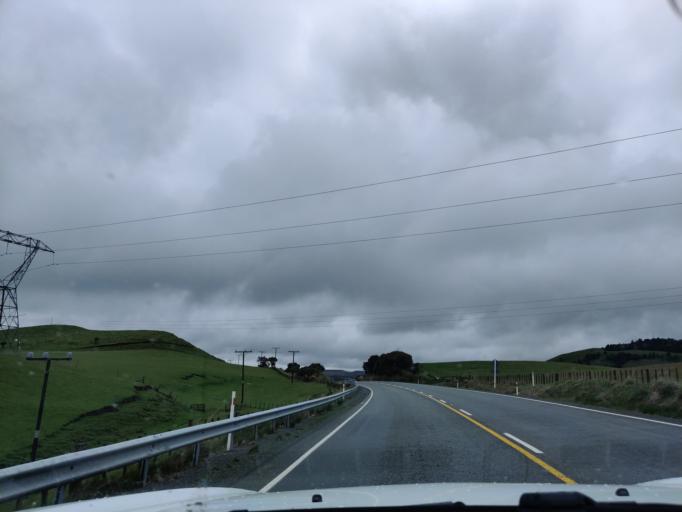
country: NZ
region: Manawatu-Wanganui
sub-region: Ruapehu District
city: Waiouru
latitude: -39.5306
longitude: 175.6831
